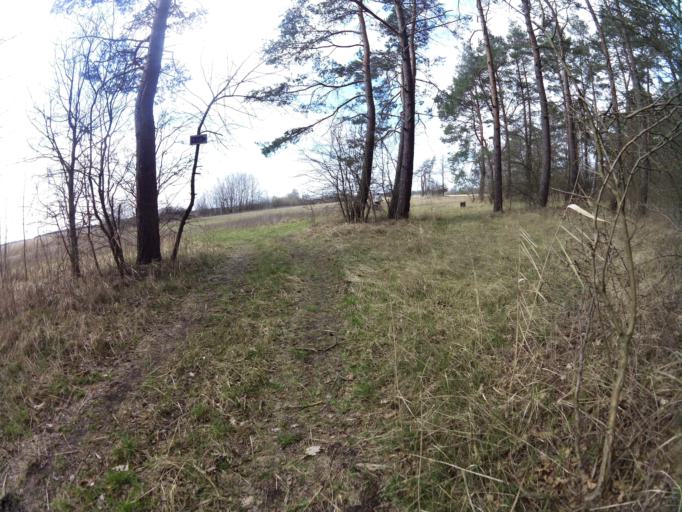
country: PL
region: West Pomeranian Voivodeship
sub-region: Powiat mysliborski
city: Mysliborz
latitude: 52.9681
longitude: 14.8815
